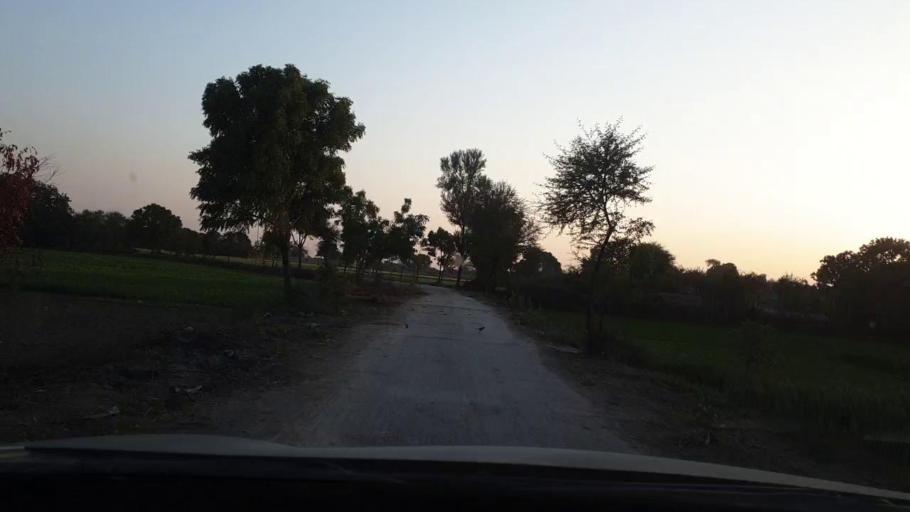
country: PK
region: Sindh
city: Tando Allahyar
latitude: 25.5252
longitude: 68.7449
